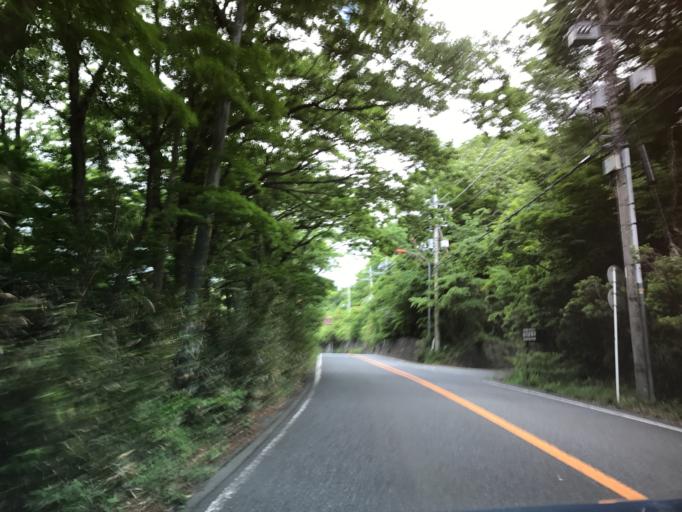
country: JP
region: Kanagawa
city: Hakone
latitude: 35.2643
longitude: 139.0232
